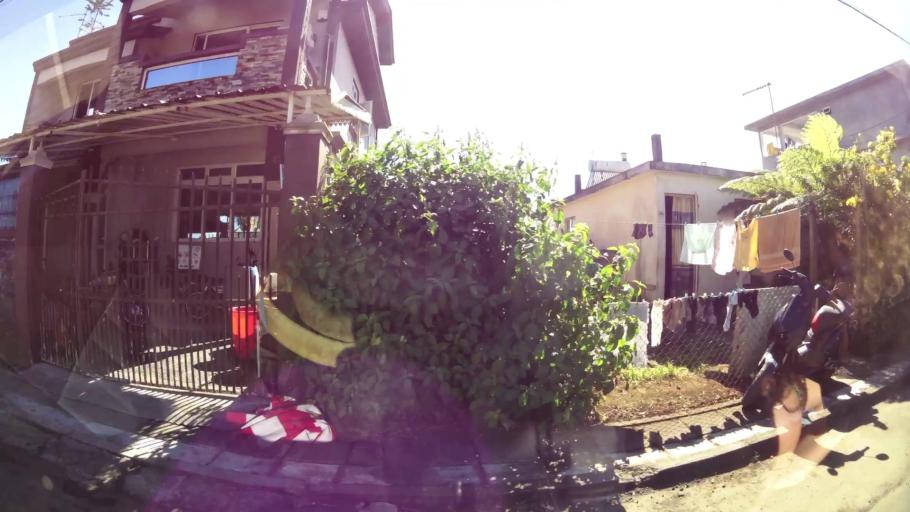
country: MU
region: Plaines Wilhems
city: Vacoas
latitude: -20.3296
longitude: 57.4846
